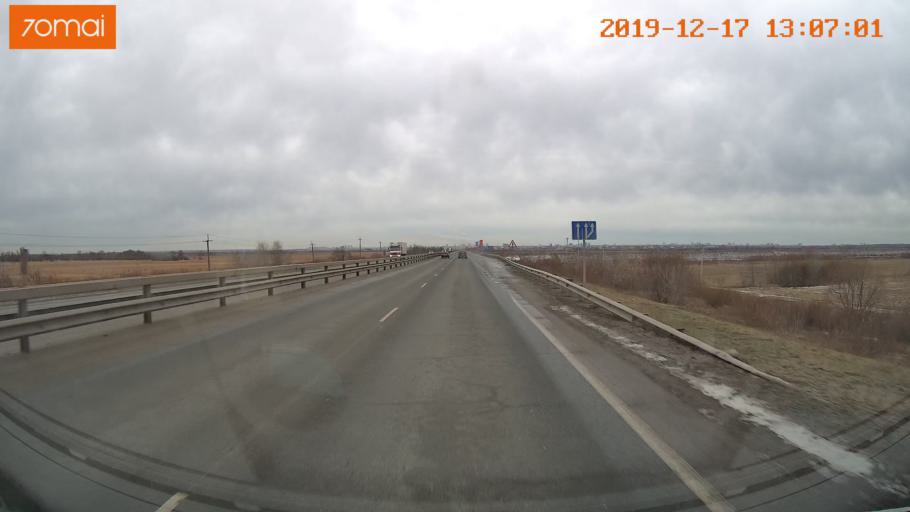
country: RU
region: Rjazan
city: Polyany
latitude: 54.6943
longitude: 39.8395
